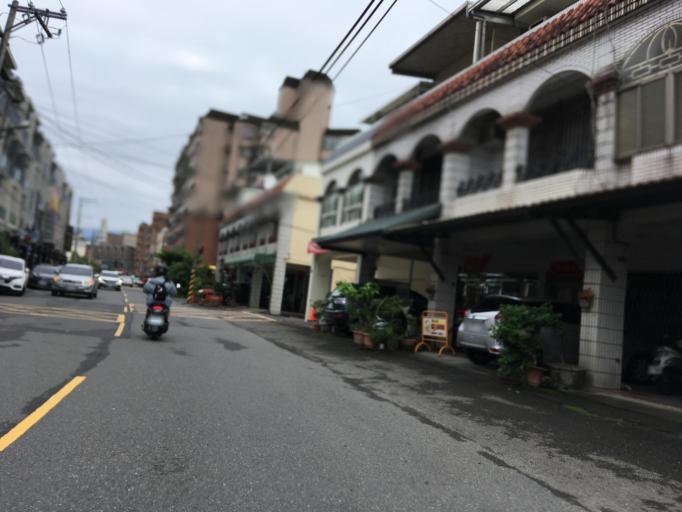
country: TW
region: Taiwan
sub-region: Yilan
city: Yilan
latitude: 24.7438
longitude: 121.7516
